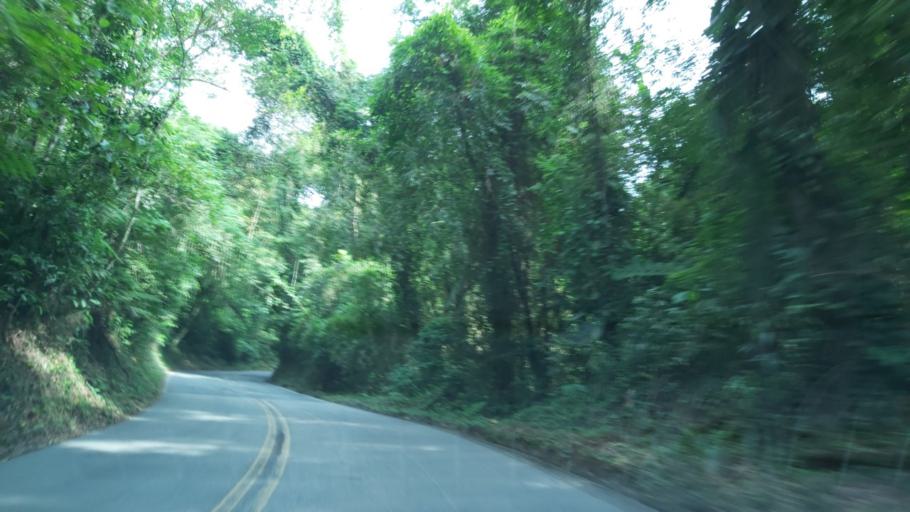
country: BR
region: Sao Paulo
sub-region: Juquia
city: Juquia
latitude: -24.0991
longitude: -47.6200
